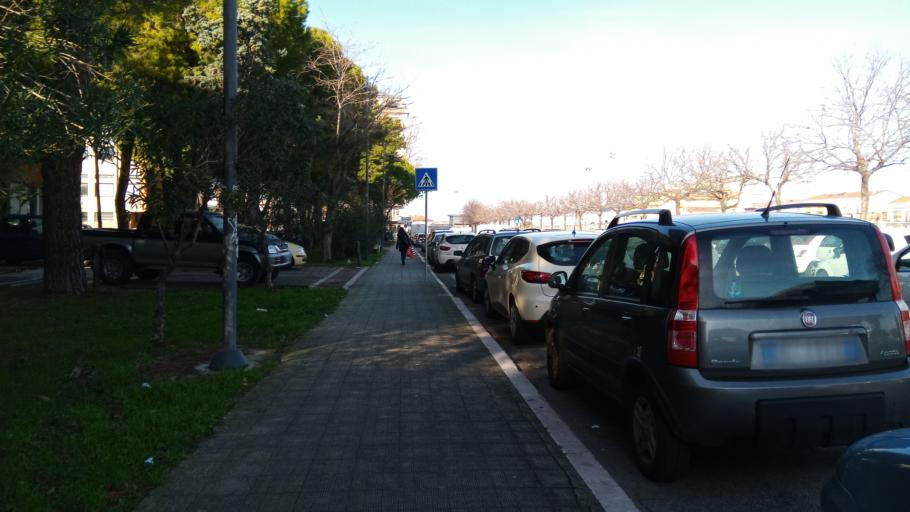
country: IT
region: Molise
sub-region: Provincia di Campobasso
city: Termoli
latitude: 42.0008
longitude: 14.9916
